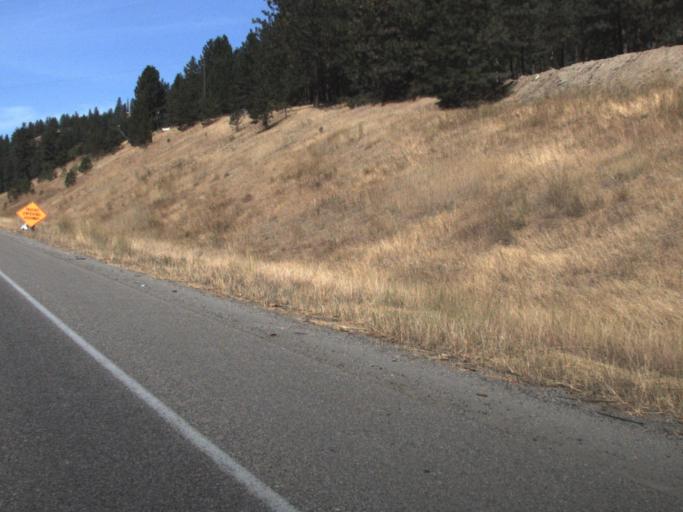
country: US
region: Washington
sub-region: Stevens County
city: Chewelah
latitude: 48.3083
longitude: -117.7829
